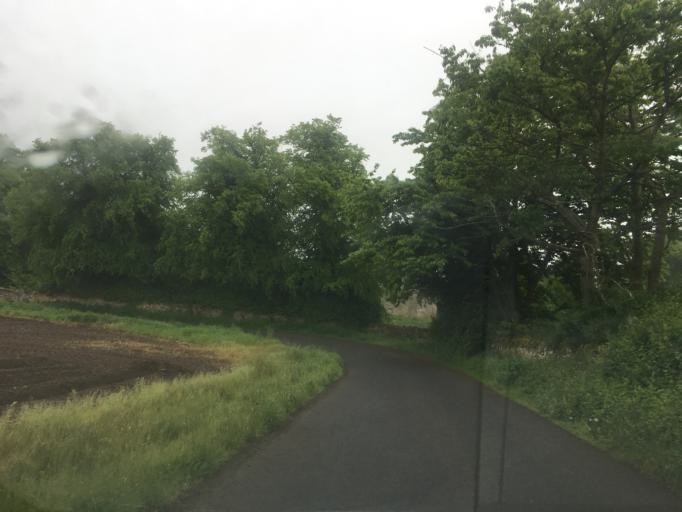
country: GB
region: Scotland
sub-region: Midlothian
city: Loanhead
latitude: 55.8969
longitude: -3.1927
